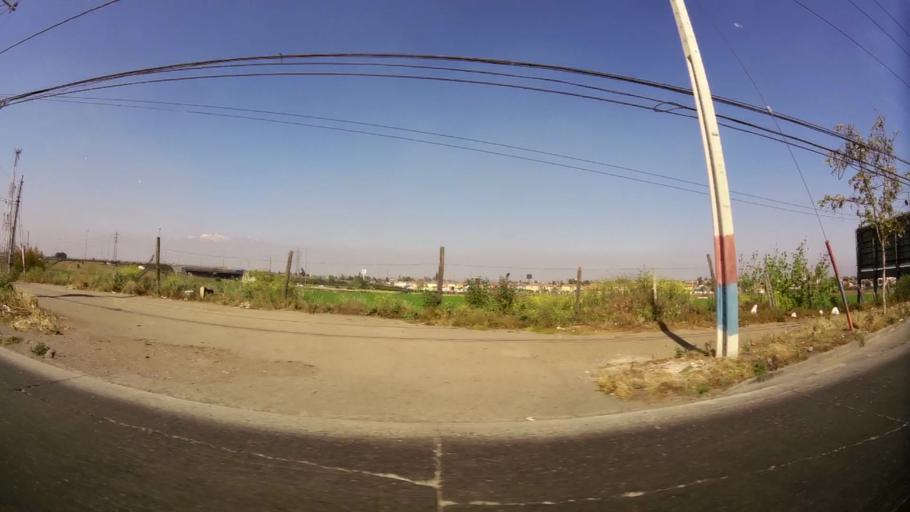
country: CL
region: Santiago Metropolitan
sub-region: Provincia de Santiago
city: Lo Prado
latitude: -33.4908
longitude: -70.7529
